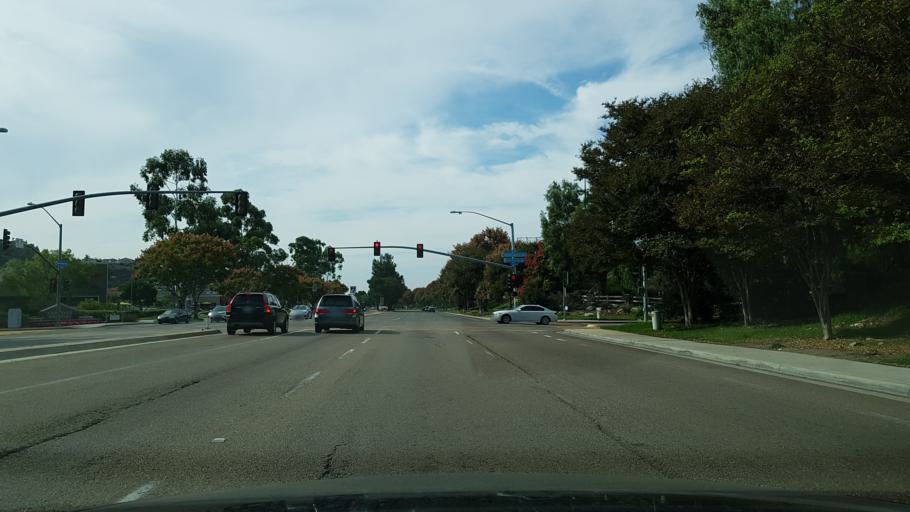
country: US
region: California
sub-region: San Diego County
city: Poway
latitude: 32.9366
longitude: -117.0958
